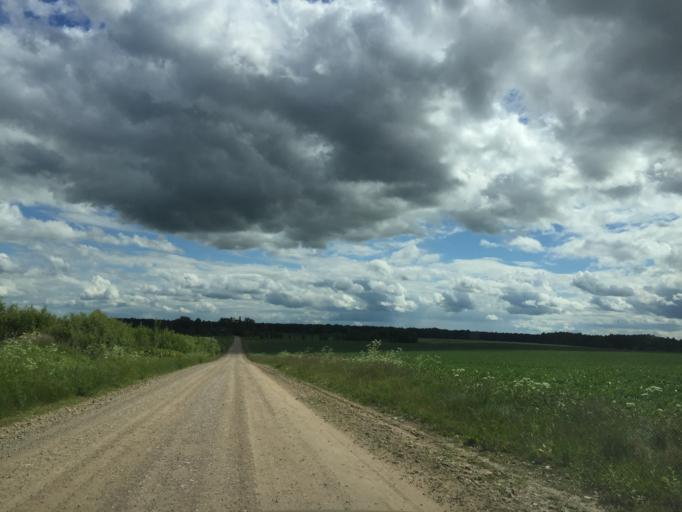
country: LV
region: Vecumnieki
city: Vecumnieki
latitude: 56.4790
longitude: 24.4165
